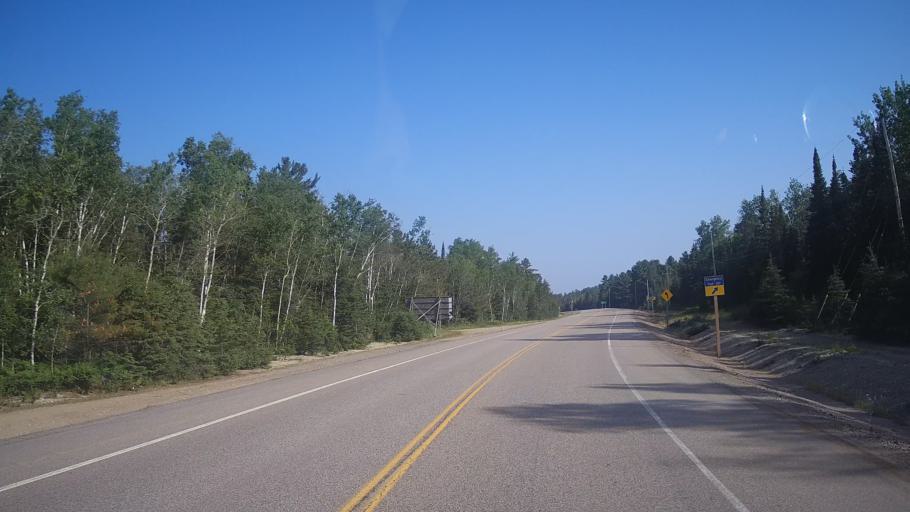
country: CA
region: Ontario
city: Rayside-Balfour
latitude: 46.7336
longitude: -81.5912
